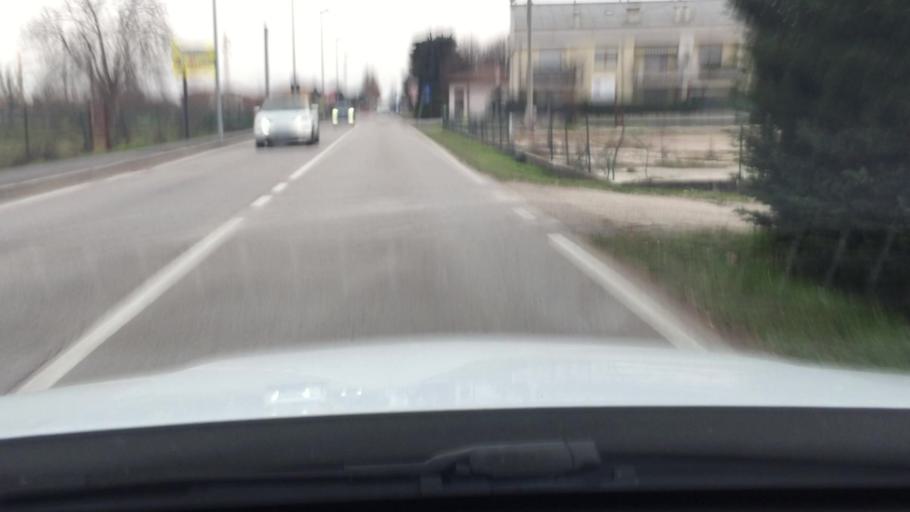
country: IT
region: Veneto
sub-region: Provincia di Verona
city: San Giovanni Lupatoto
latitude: 45.3781
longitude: 11.0288
